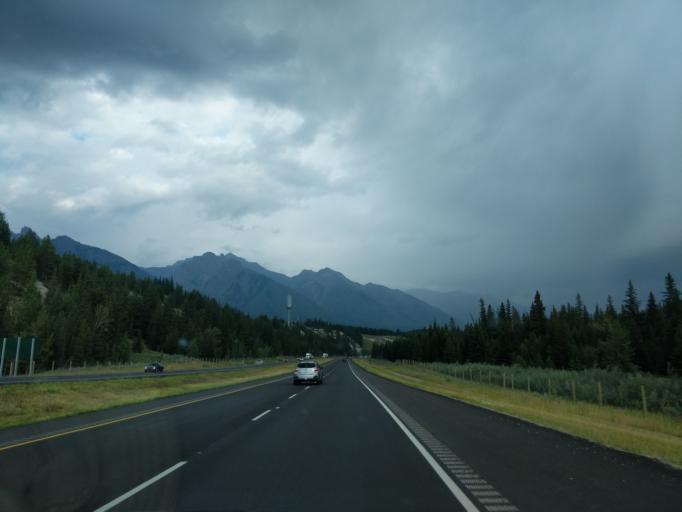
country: CA
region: Alberta
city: Banff
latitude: 51.2019
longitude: -115.5158
